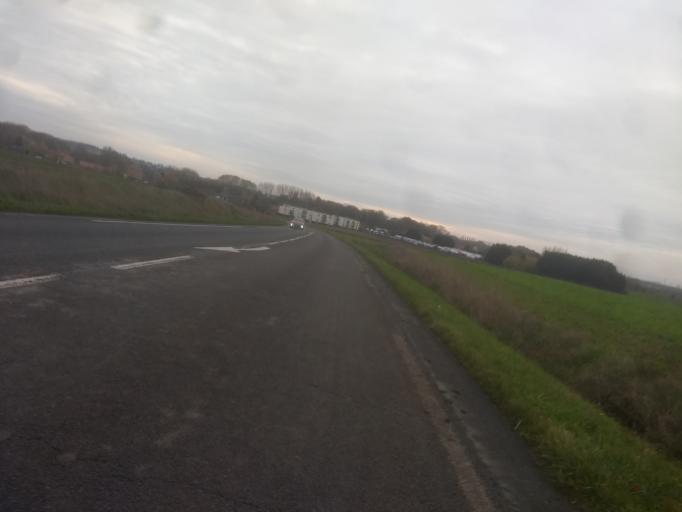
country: FR
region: Nord-Pas-de-Calais
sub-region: Departement du Pas-de-Calais
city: Achicourt
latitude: 50.2697
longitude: 2.7473
